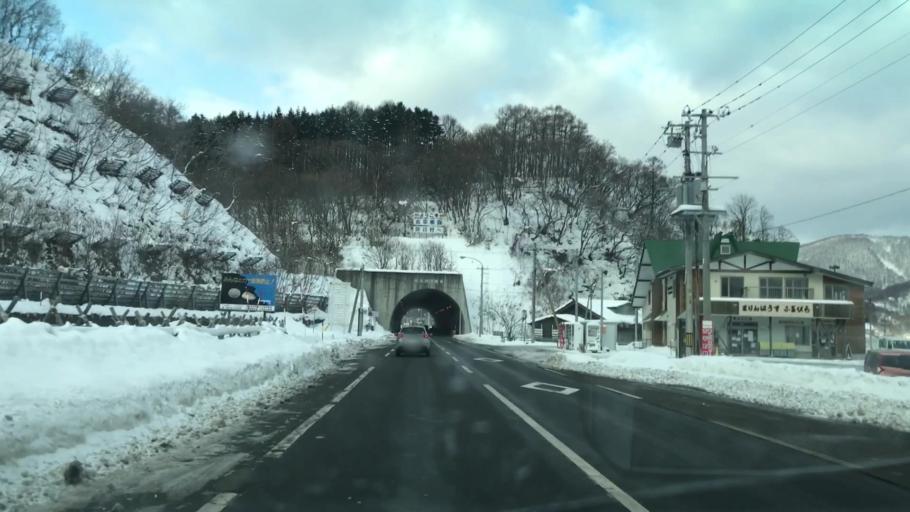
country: JP
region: Hokkaido
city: Yoichi
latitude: 43.2602
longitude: 140.6551
